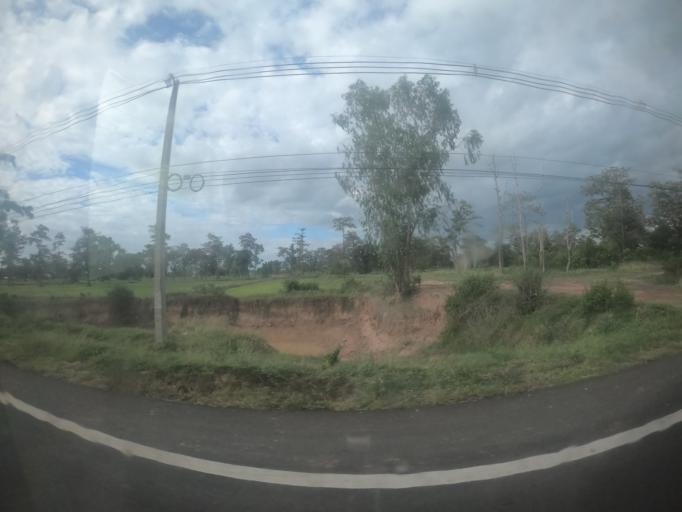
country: TH
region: Surin
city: Prasat
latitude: 14.5744
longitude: 103.4840
